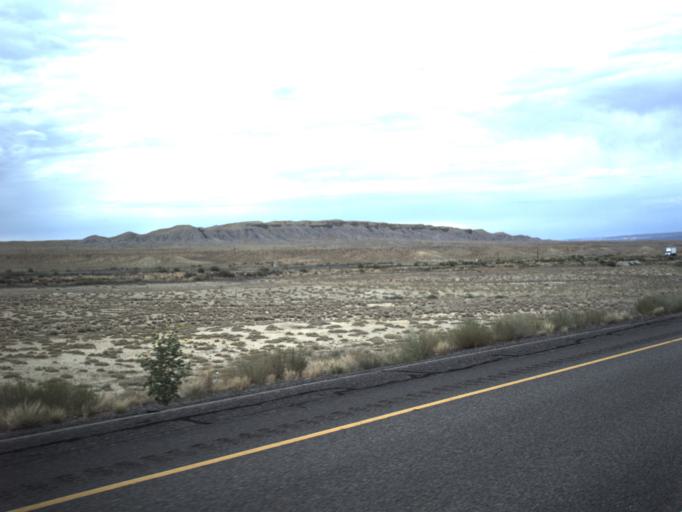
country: US
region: Utah
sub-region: Grand County
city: Moab
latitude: 38.9375
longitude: -109.4898
